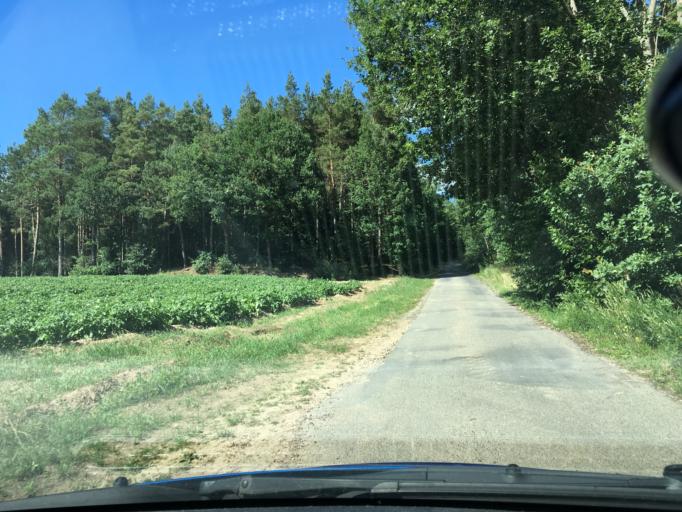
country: DE
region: Lower Saxony
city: Neu Darchau
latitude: 53.1901
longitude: 10.8944
